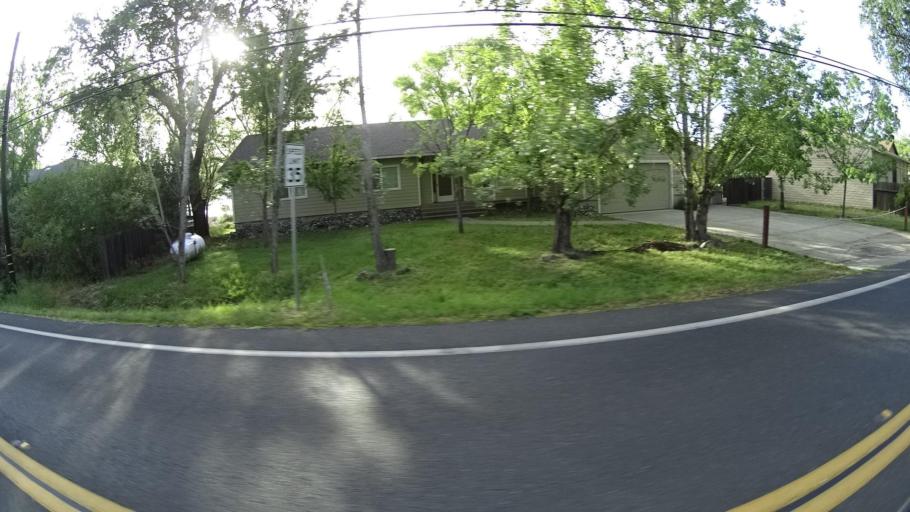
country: US
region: California
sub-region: Lake County
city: North Lakeport
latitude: 39.0972
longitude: -122.8999
